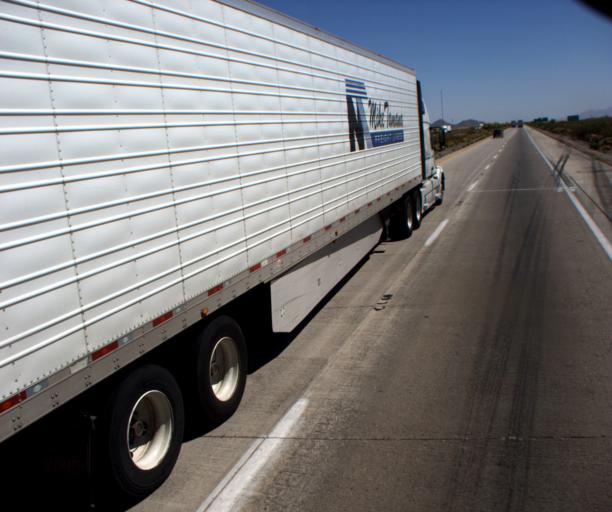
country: US
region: Arizona
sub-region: Maricopa County
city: Buckeye
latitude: 33.4452
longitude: -112.7049
